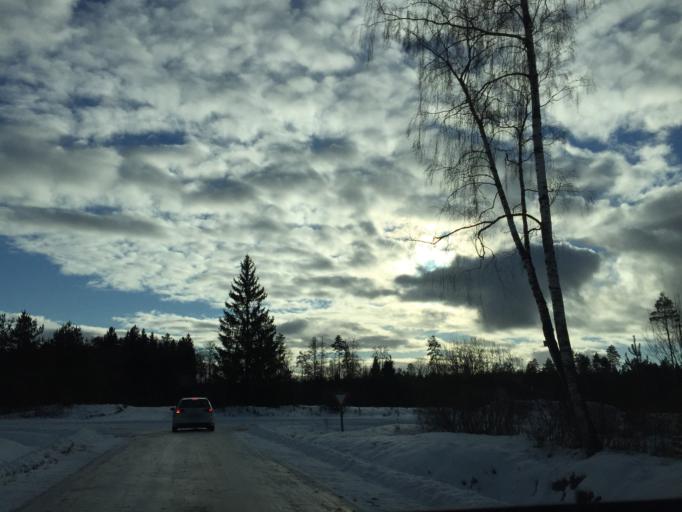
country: LV
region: Ogre
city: Jumprava
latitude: 56.5480
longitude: 24.8593
